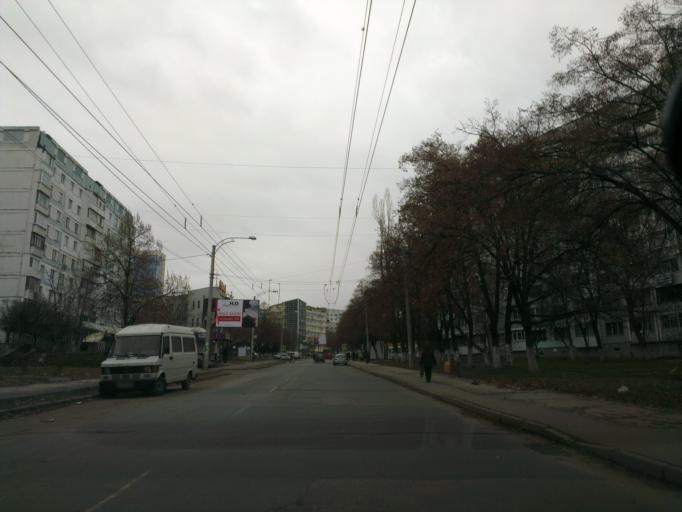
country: MD
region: Chisinau
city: Chisinau
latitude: 46.9775
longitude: 28.8599
